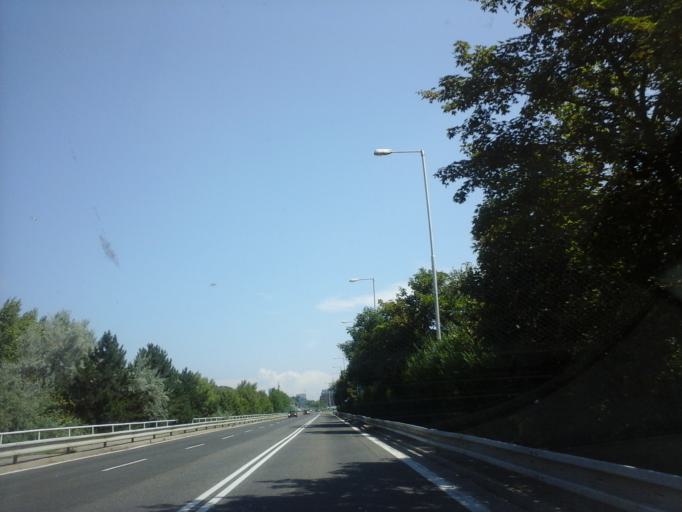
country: SK
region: Bratislavsky
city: Bratislava
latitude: 48.1275
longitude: 17.0908
